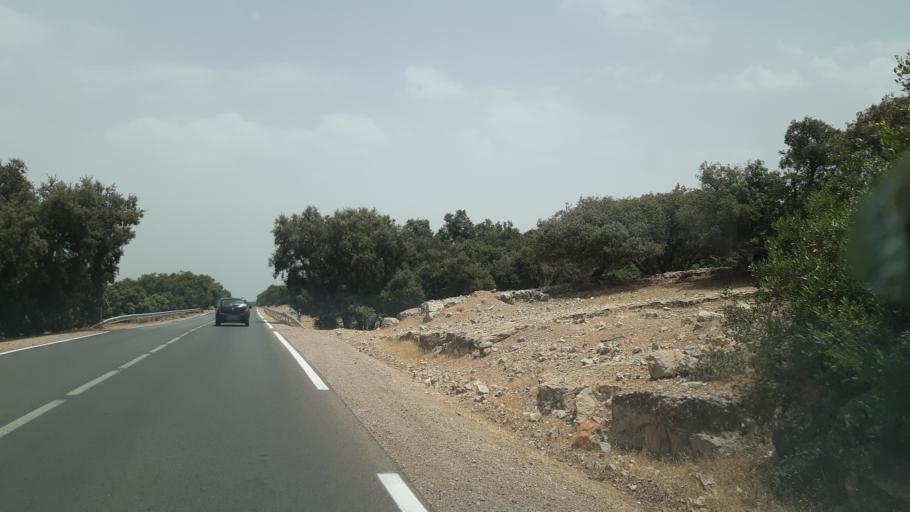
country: MA
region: Meknes-Tafilalet
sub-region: Ifrane
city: Ifrane
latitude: 33.6554
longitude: -5.0604
